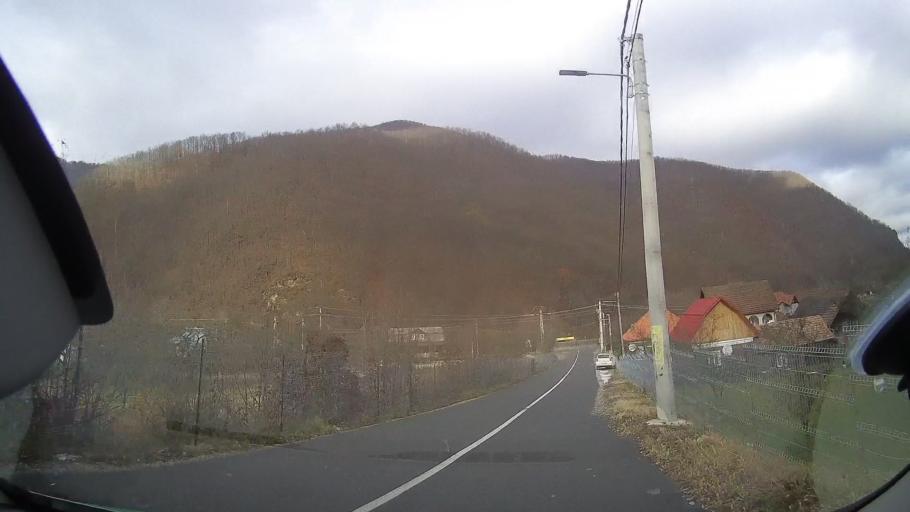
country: RO
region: Cluj
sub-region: Comuna Valea Ierii
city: Valea Ierii
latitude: 46.6904
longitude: 23.3077
